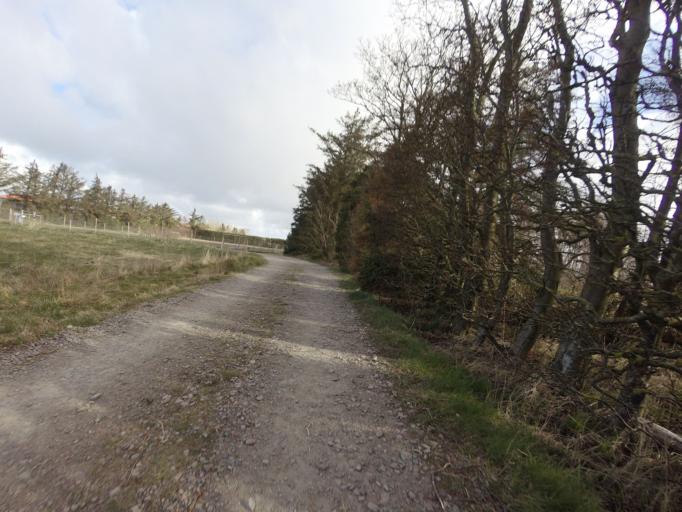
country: SE
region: Skane
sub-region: Hoganas Kommun
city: Hoganas
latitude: 56.1537
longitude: 12.5861
